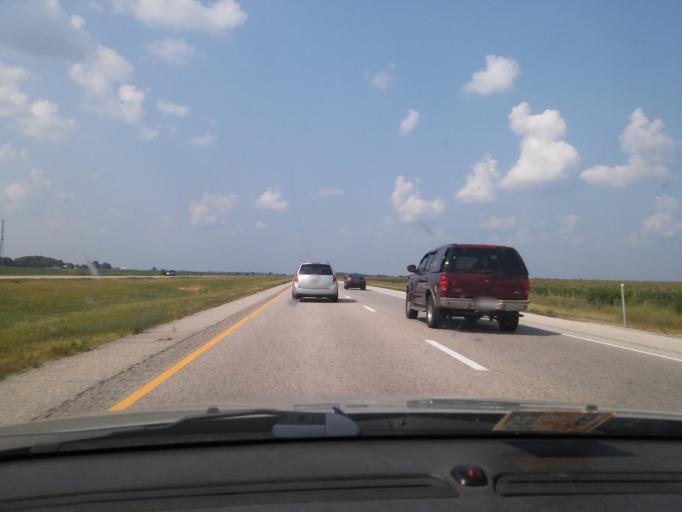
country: US
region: Illinois
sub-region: McLean County
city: Chenoa
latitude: 40.8079
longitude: -88.6973
